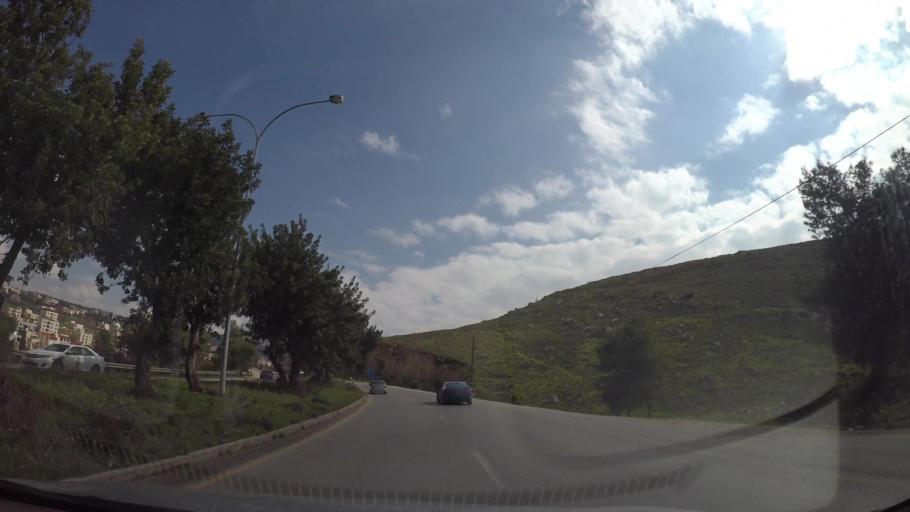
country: JO
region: Balqa
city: As Salt
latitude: 32.0319
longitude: 35.7937
